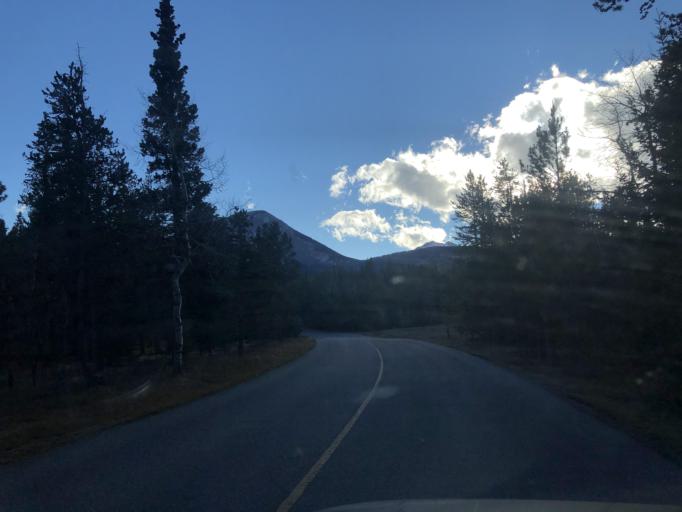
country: CA
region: Alberta
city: Canmore
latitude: 51.0782
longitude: -115.0780
